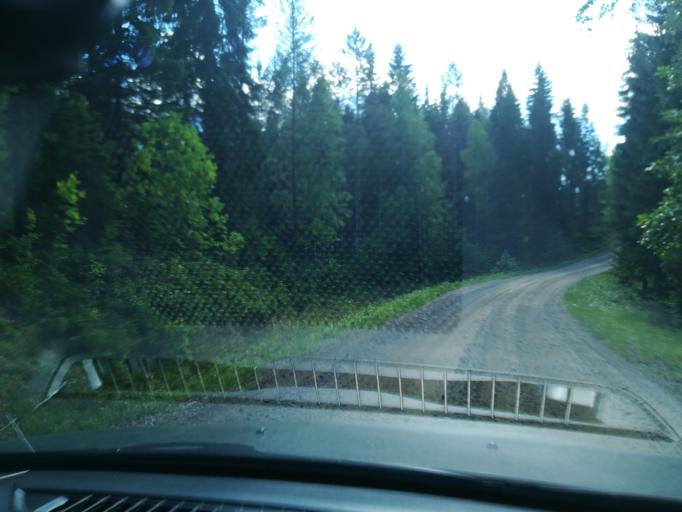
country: FI
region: Southern Savonia
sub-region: Mikkeli
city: Puumala
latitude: 61.6498
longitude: 28.1846
